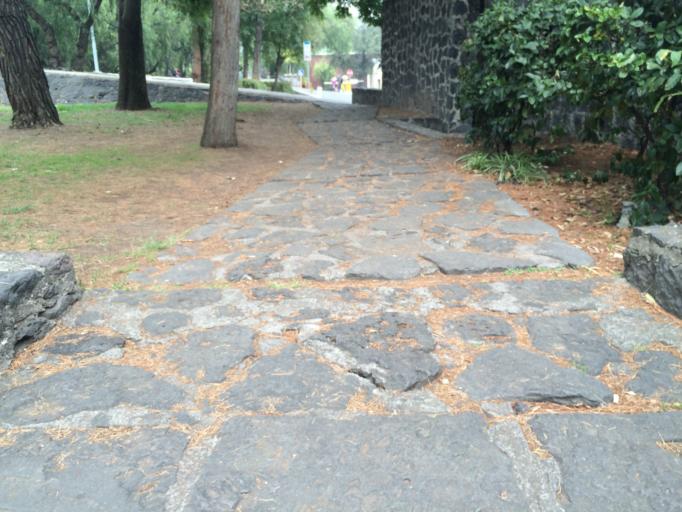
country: MX
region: Mexico City
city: Coyoacan
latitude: 19.3304
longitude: -99.1835
